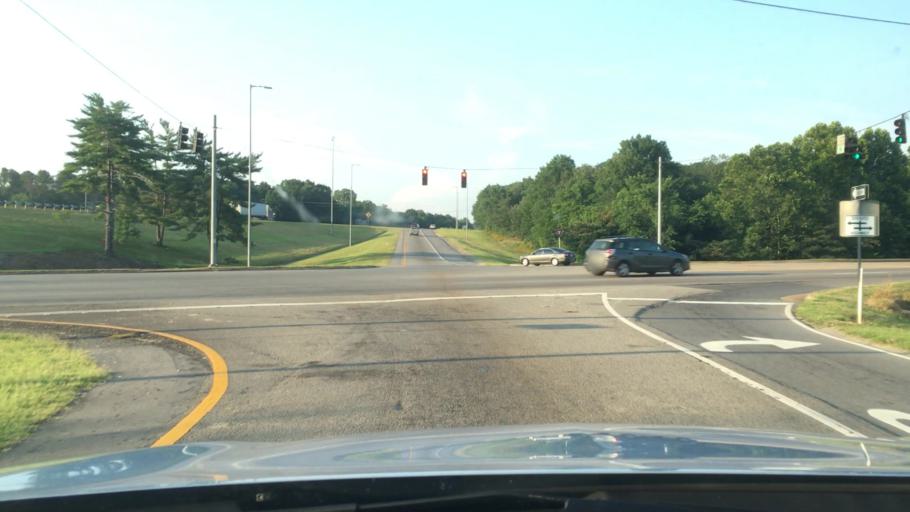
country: US
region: Alabama
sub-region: DeKalb County
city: Fort Payne
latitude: 34.4368
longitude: -85.7480
